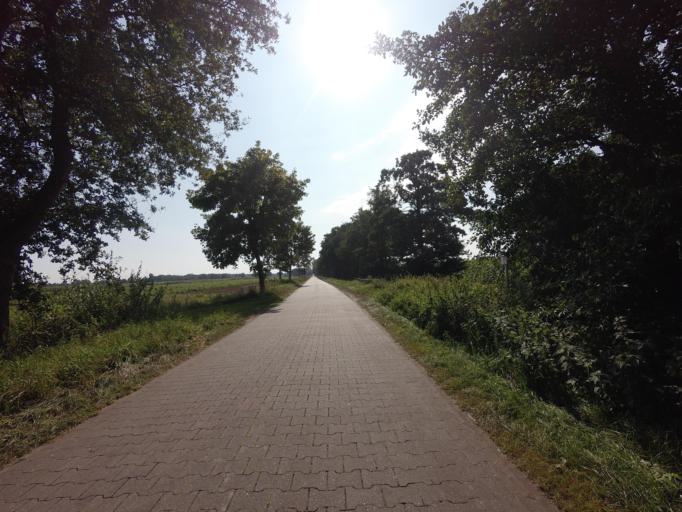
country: DE
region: Lower Saxony
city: Wilsum
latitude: 52.5696
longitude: 6.8222
